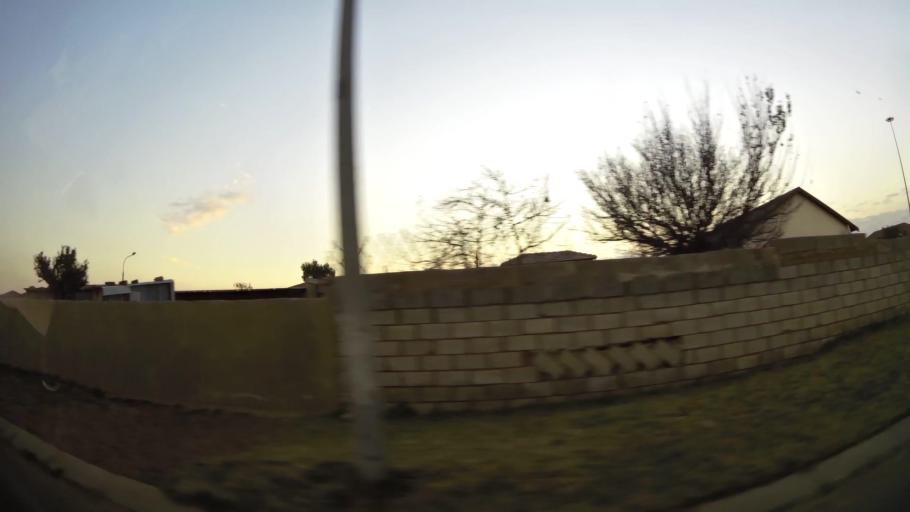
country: ZA
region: Gauteng
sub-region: West Rand District Municipality
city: Randfontein
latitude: -26.2124
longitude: 27.7139
